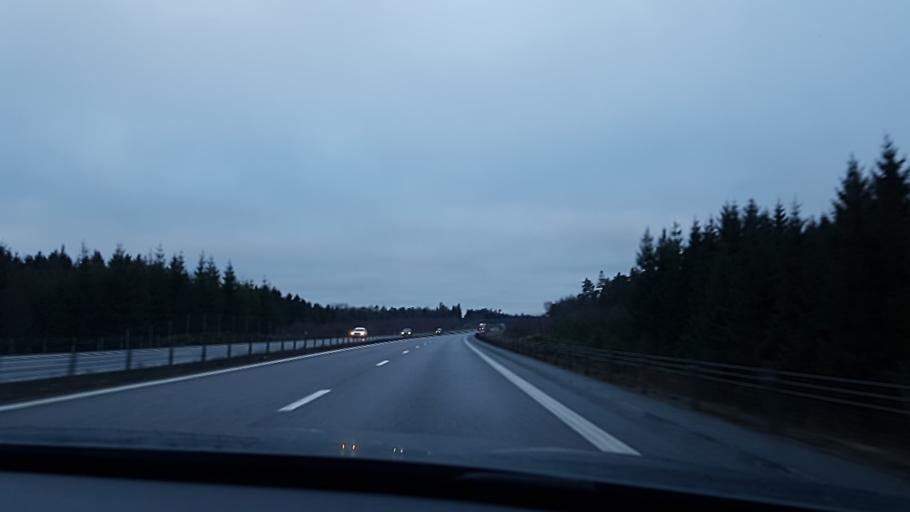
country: SE
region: Skane
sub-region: Orkelljunga Kommun
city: OErkelljunga
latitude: 56.3336
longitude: 13.4528
